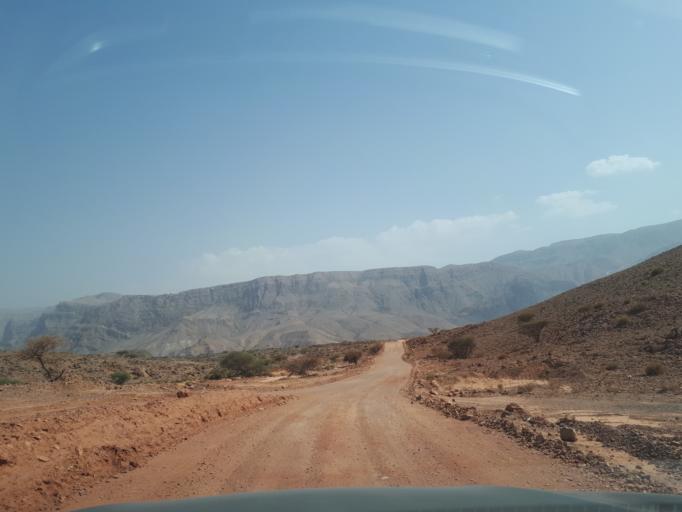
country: OM
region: Ash Sharqiyah
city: Al Qabil
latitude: 23.0750
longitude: 58.9573
